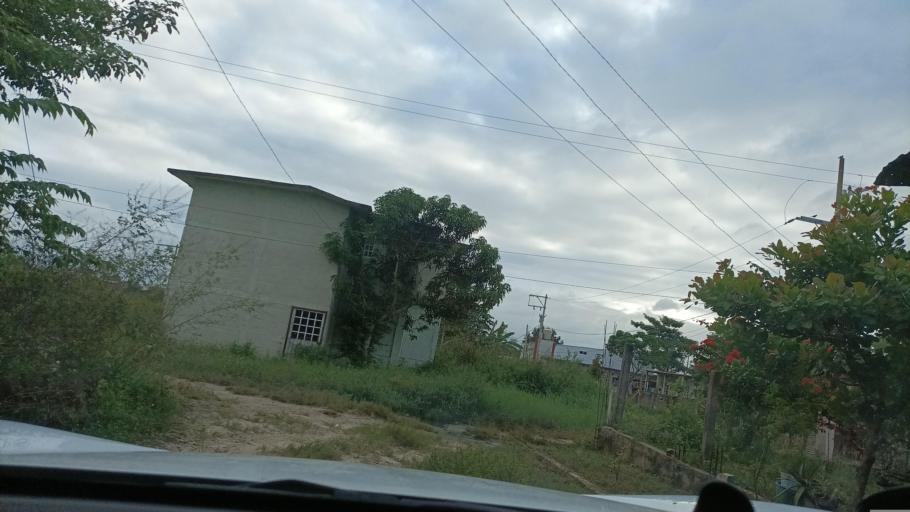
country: MX
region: Veracruz
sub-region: Cosoleacaque
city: Hermenegildo J. Aldana
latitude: 17.9951
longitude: -94.6092
